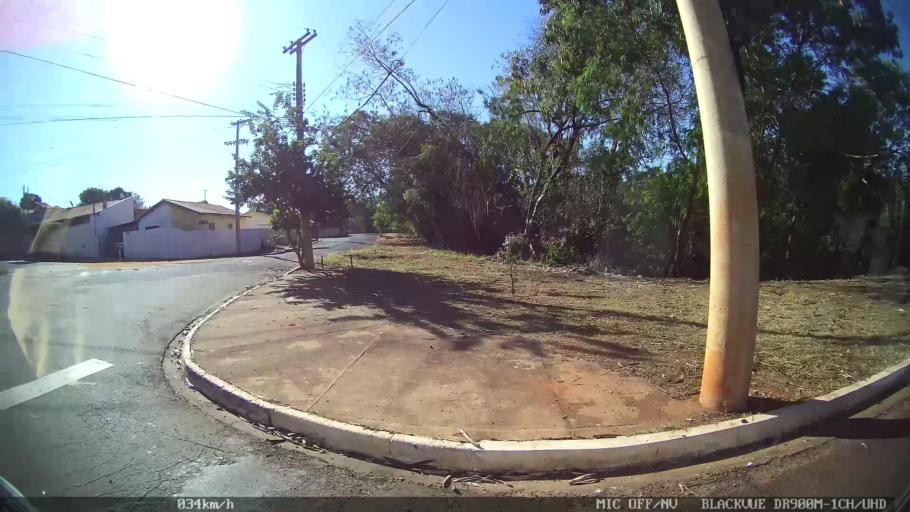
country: BR
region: Sao Paulo
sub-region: Olimpia
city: Olimpia
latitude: -20.7407
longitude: -48.8849
